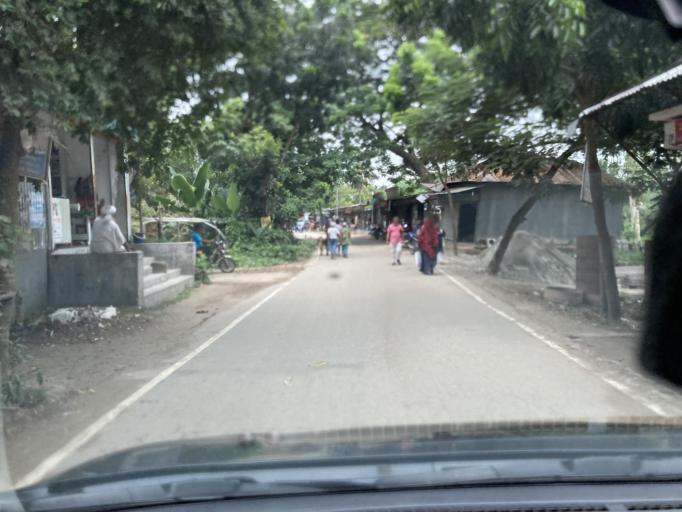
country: BD
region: Dhaka
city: Dohar
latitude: 23.7619
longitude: 90.1941
